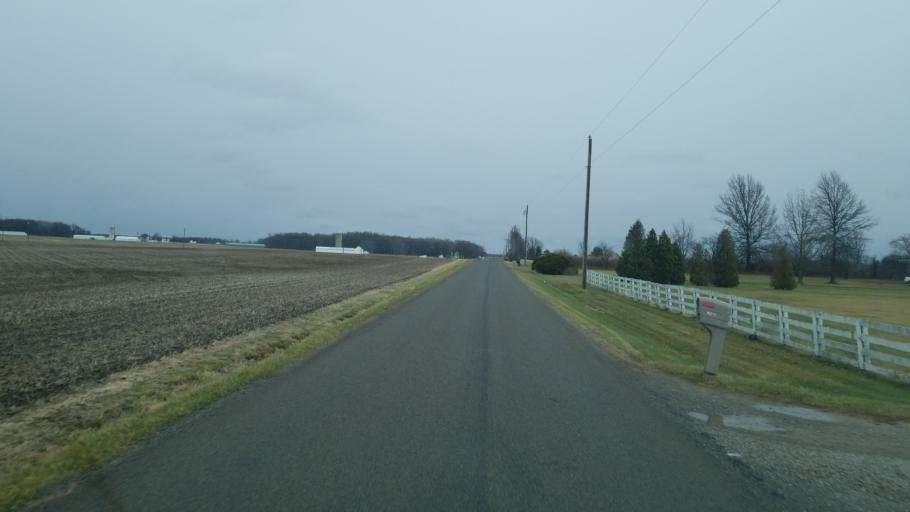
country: US
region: Ohio
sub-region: Union County
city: Marysville
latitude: 40.3305
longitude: -83.3624
